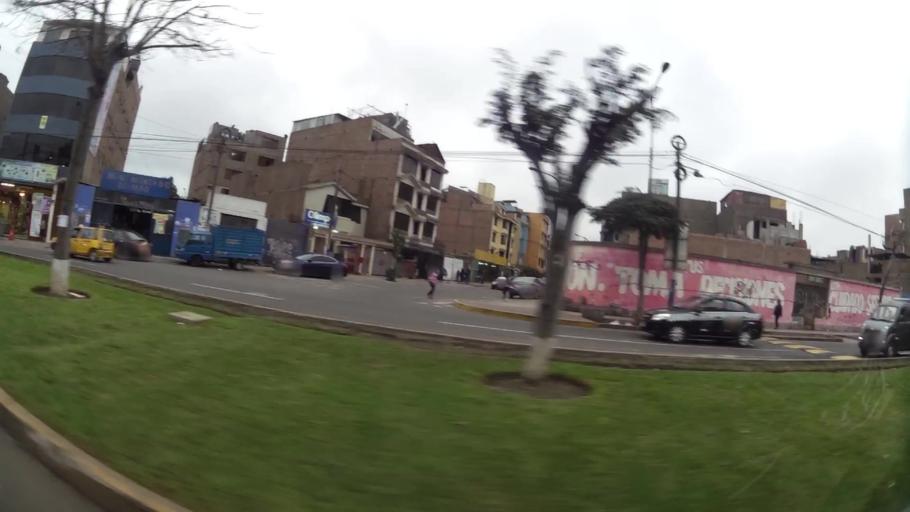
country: PE
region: Lima
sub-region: Lima
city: San Luis
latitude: -12.0749
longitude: -76.9784
